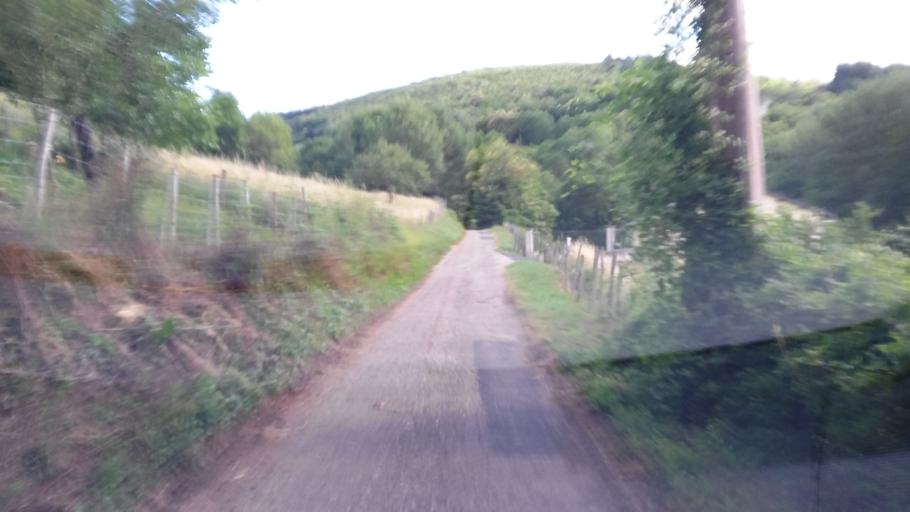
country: FR
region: Languedoc-Roussillon
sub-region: Departement de la Lozere
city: Meyrueis
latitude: 44.0180
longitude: 3.3614
